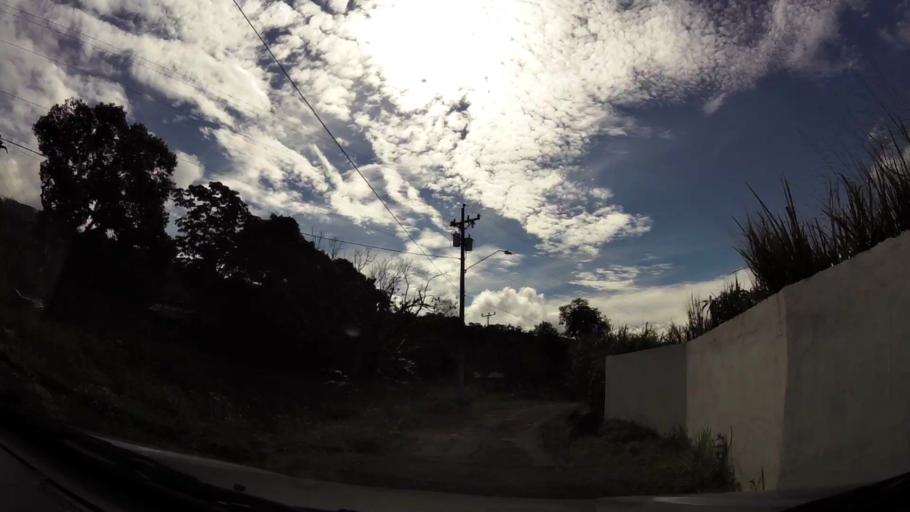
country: PA
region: Chiriqui
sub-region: Distrito Boquete
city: Boquete
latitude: 8.7749
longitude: -82.4335
